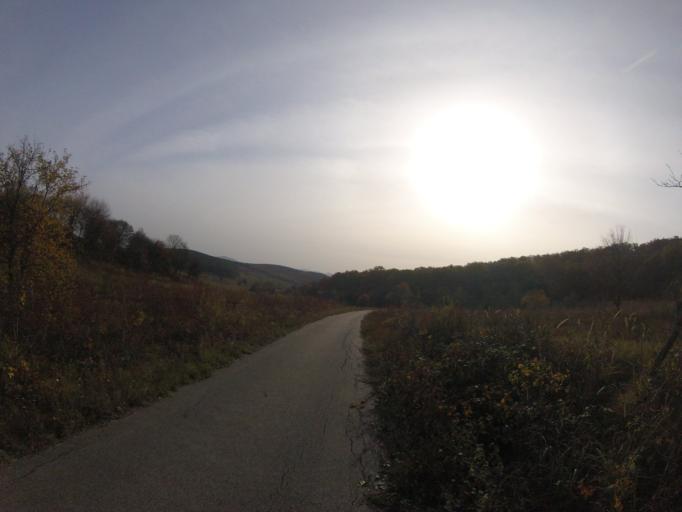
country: HU
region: Borsod-Abauj-Zemplen
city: Gonc
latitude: 48.5210
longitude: 21.4572
